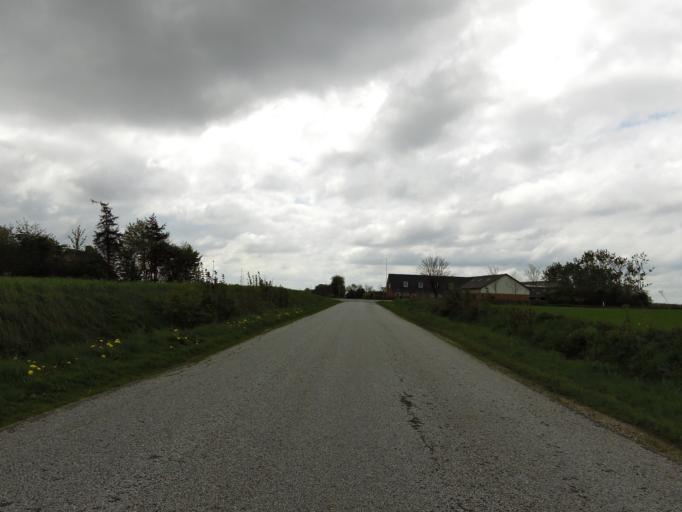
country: DK
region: South Denmark
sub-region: Haderslev Kommune
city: Gram
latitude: 55.2298
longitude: 8.9896
